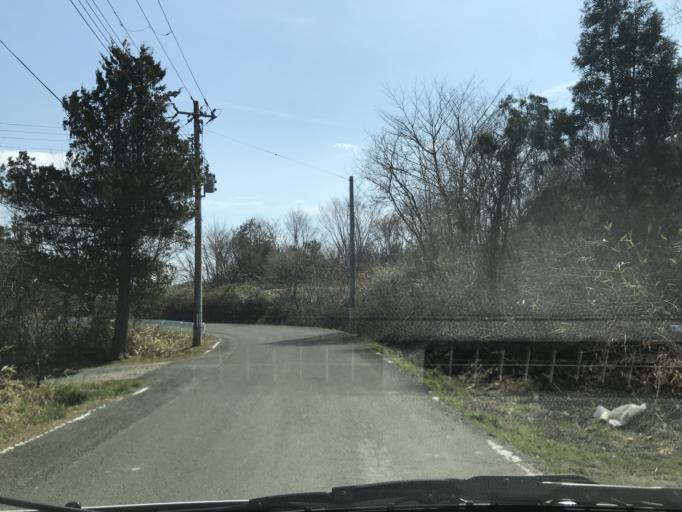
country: JP
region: Iwate
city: Ichinoseki
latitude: 38.8376
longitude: 141.1043
